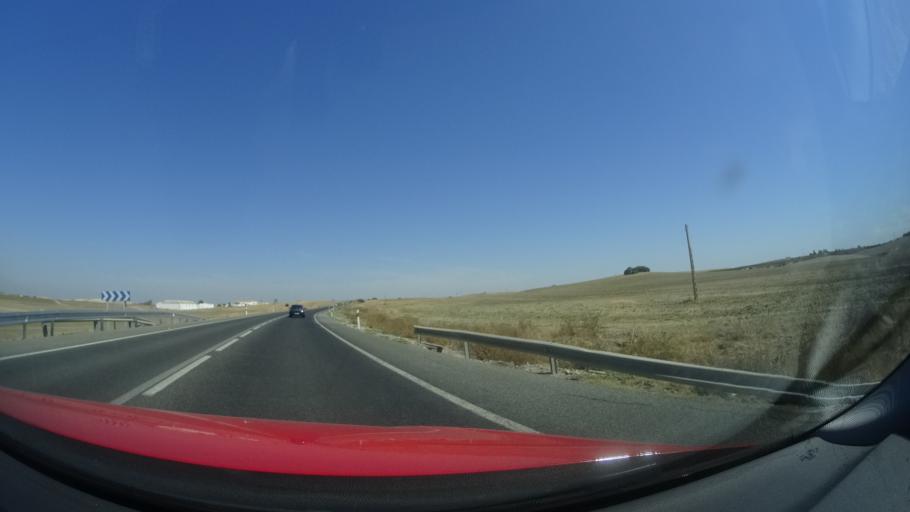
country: ES
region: Andalusia
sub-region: Provincia de Sevilla
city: Las Cabezas de San Juan
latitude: 36.9341
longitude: -5.9228
